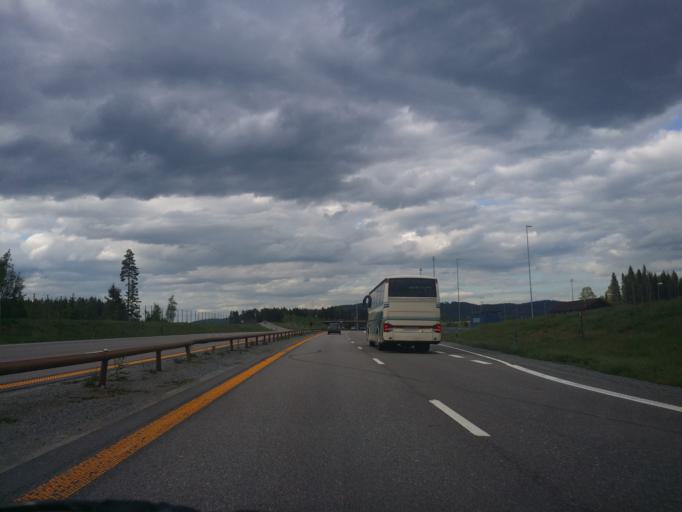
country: NO
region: Akershus
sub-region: Eidsvoll
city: Eidsvoll
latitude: 60.3864
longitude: 11.2127
